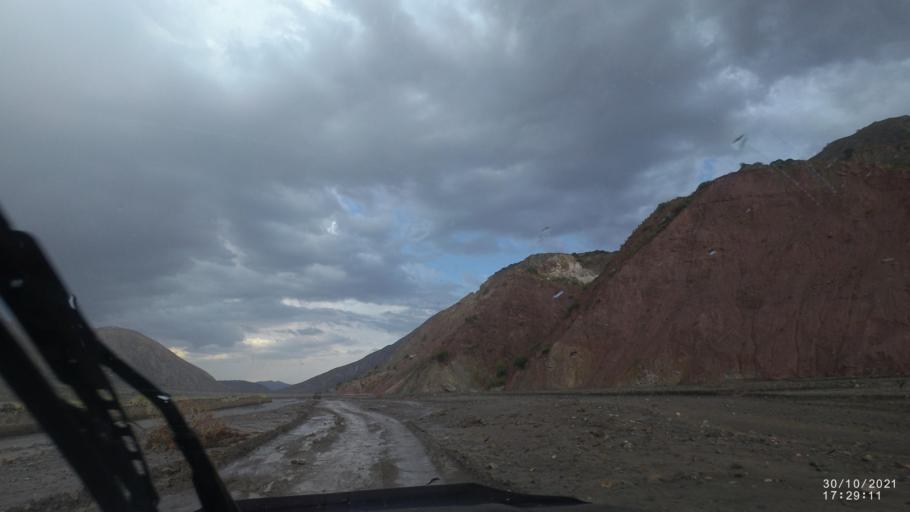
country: BO
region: Cochabamba
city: Sipe Sipe
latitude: -17.5233
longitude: -66.6033
